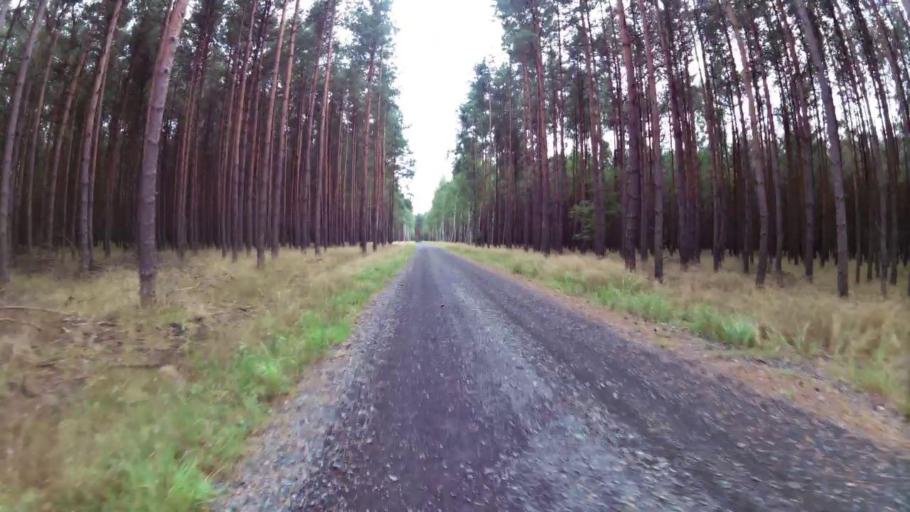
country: PL
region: West Pomeranian Voivodeship
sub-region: Powiat mysliborski
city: Debno
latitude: 52.7847
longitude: 14.7209
